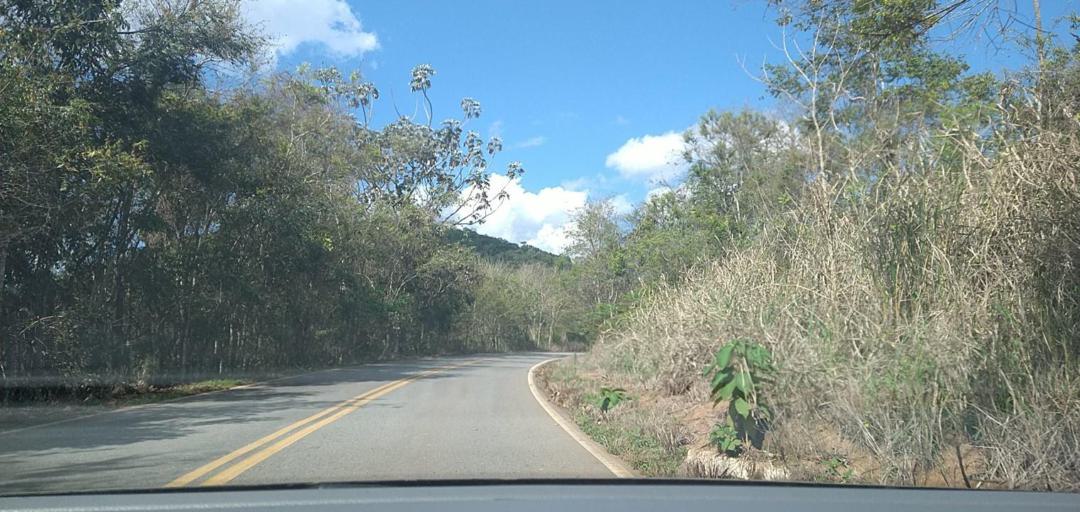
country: BR
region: Minas Gerais
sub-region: Alvinopolis
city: Alvinopolis
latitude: -20.0151
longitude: -43.0864
